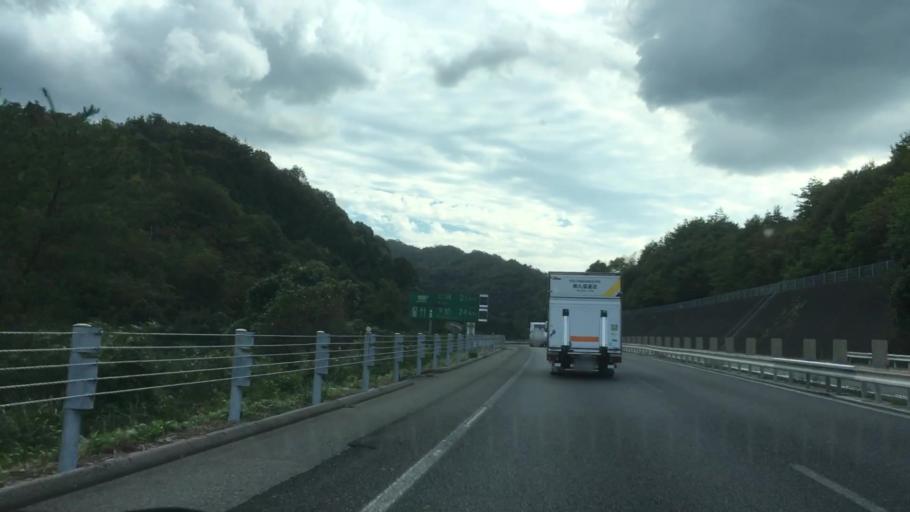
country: JP
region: Yamaguchi
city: Iwakuni
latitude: 34.1273
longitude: 132.1113
